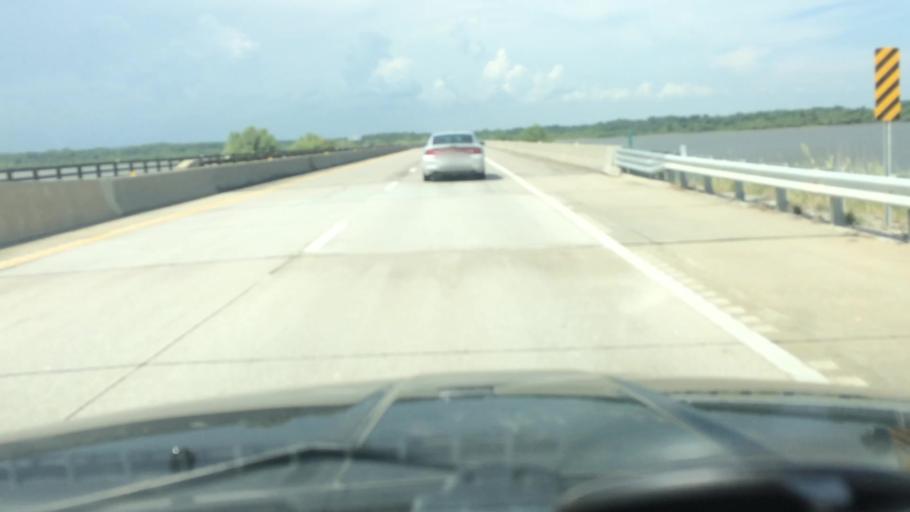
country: US
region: Missouri
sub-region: Henry County
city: Clinton
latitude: 38.2755
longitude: -93.7598
